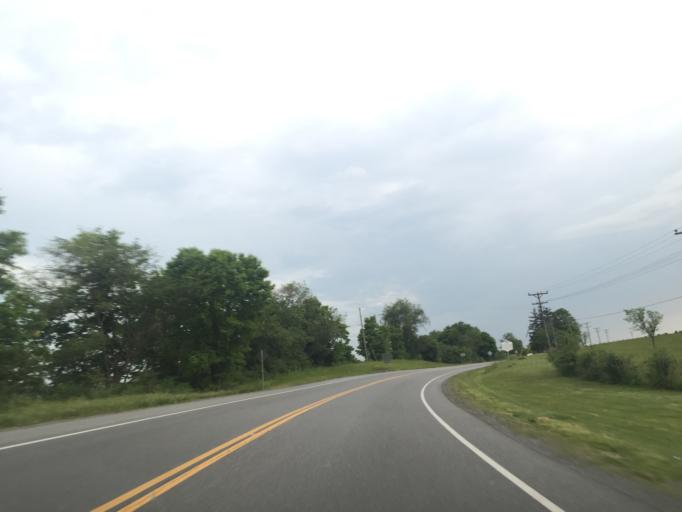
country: US
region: Virginia
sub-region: Clarke County
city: Berryville
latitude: 39.1927
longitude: -77.9182
